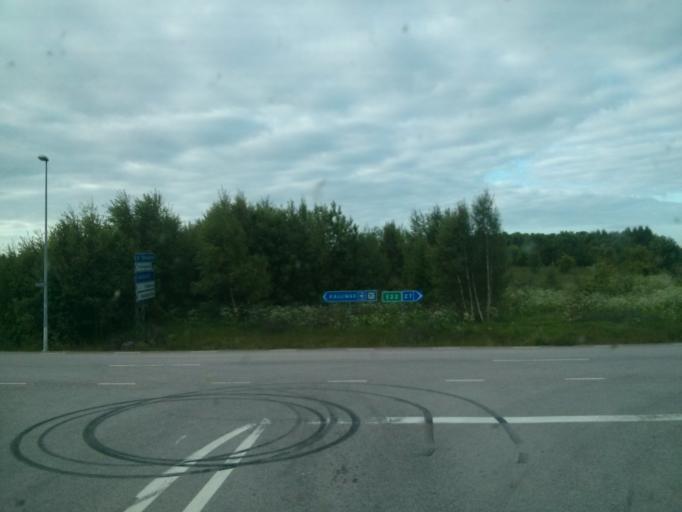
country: SE
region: Blekinge
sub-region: Ronneby Kommun
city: Kallinge
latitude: 56.2545
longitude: 15.2579
